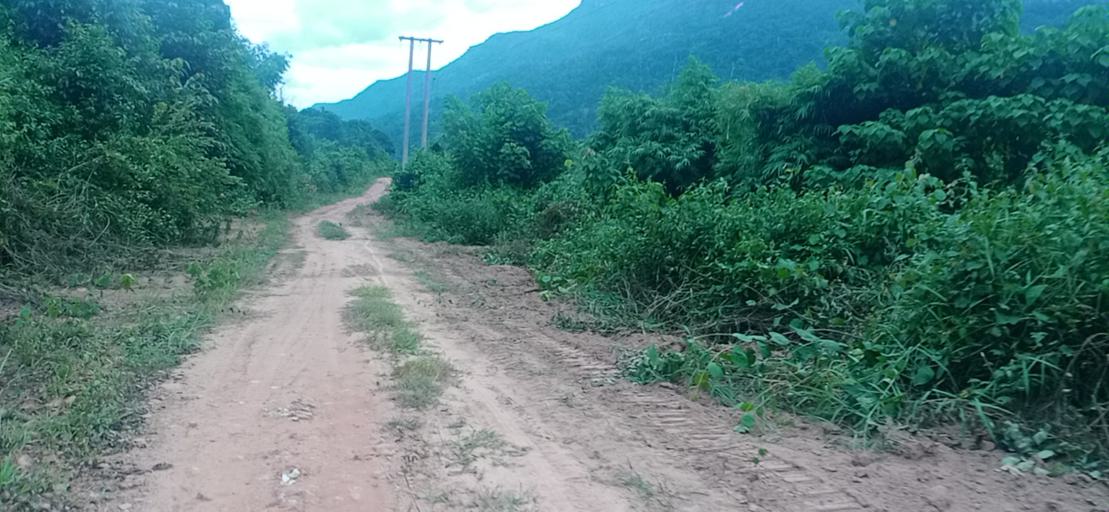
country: TH
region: Changwat Bueng Kan
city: Pak Khat
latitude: 18.5597
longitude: 103.2314
